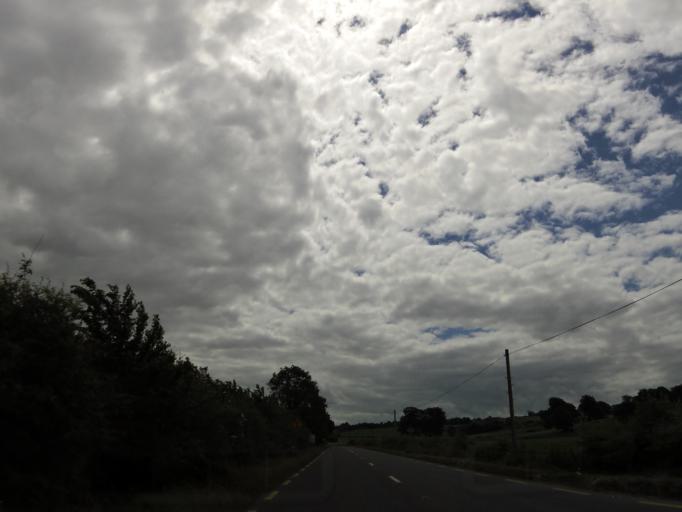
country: IE
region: Munster
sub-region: North Tipperary
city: Nenagh
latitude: 52.7761
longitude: -8.0291
